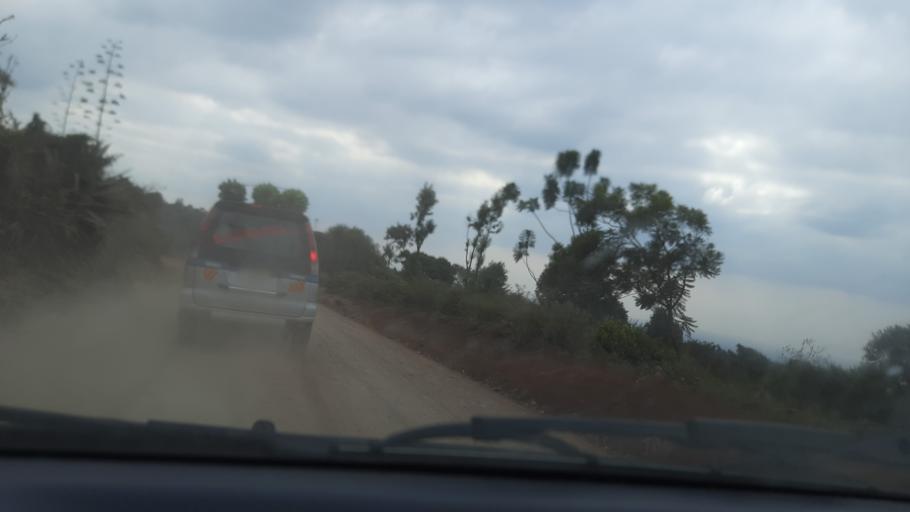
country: TZ
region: Kilimanjaro
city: Moshi
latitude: -2.8760
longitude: 37.3605
